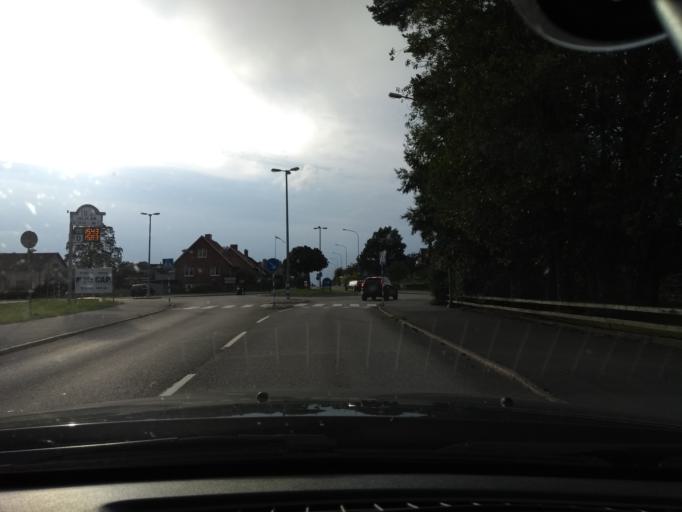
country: SE
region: Joenkoeping
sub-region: Nassjo Kommun
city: Nassjo
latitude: 57.6477
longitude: 14.7222
